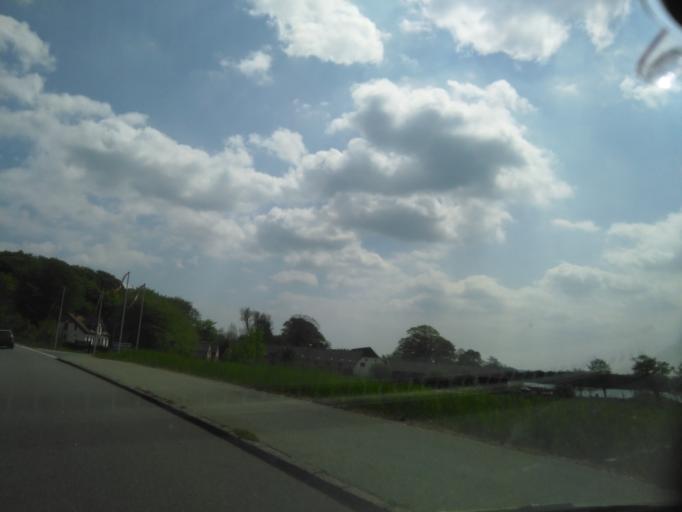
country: DK
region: Central Jutland
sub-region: Skanderborg Kommune
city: Skanderborg
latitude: 56.0301
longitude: 9.9570
